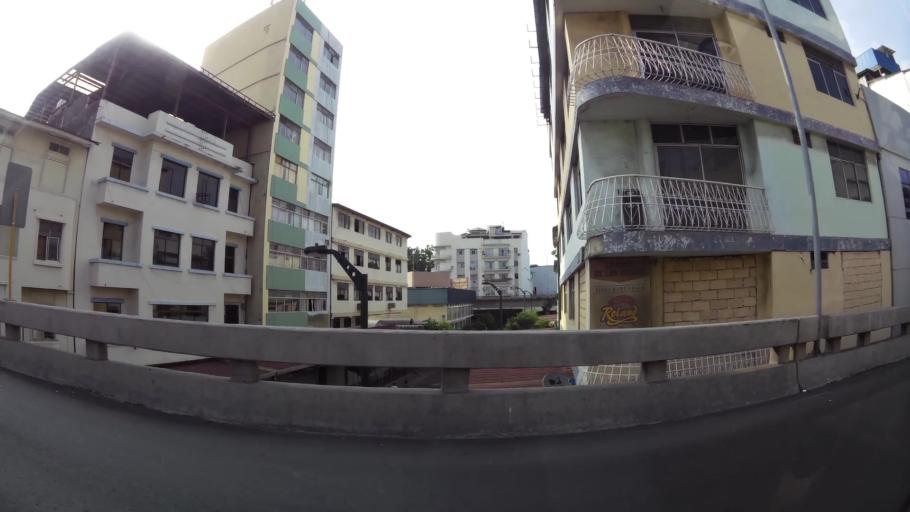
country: EC
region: Guayas
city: Guayaquil
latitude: -2.2002
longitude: -79.8841
